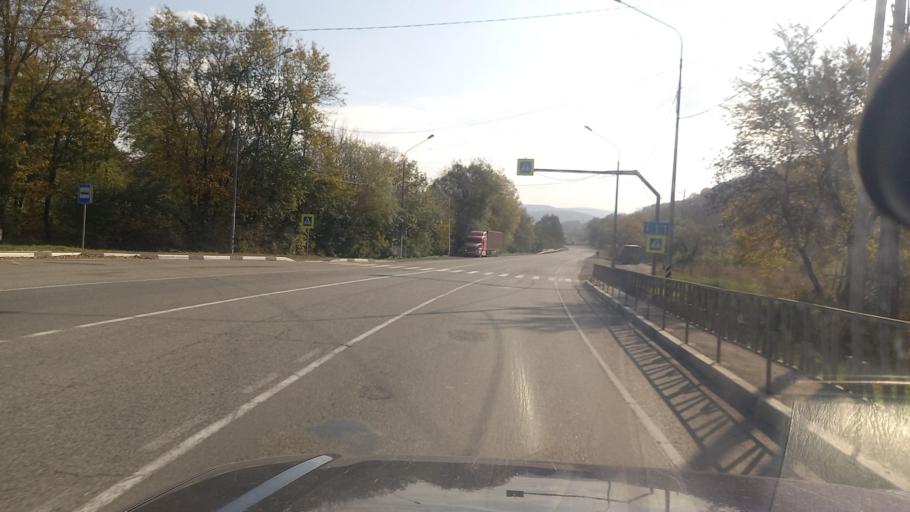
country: RU
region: Krasnodarskiy
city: Verkhnebakanskiy
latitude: 44.8455
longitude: 37.6855
